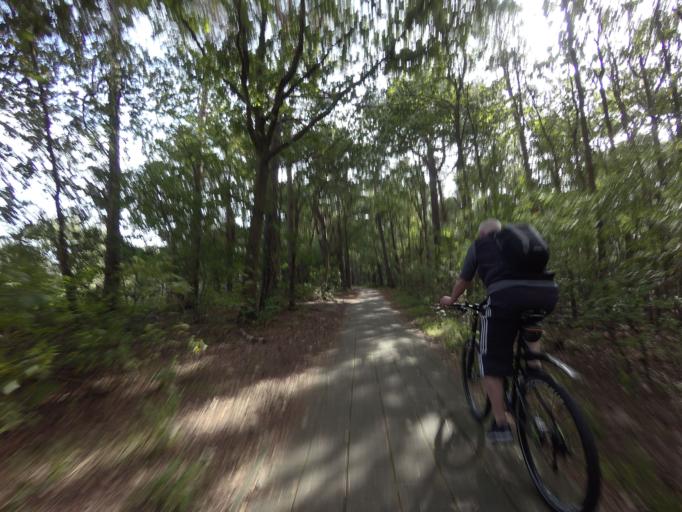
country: NL
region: North Holland
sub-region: Gemeente Texel
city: Den Burg
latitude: 53.0797
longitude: 4.7592
